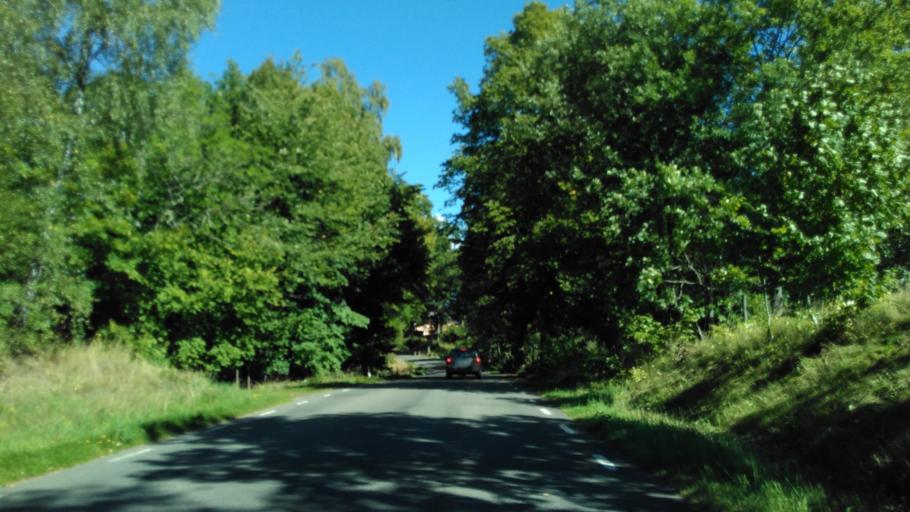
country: SE
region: Vaestra Goetaland
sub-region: Skara Kommun
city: Axvall
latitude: 58.4379
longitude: 13.6509
